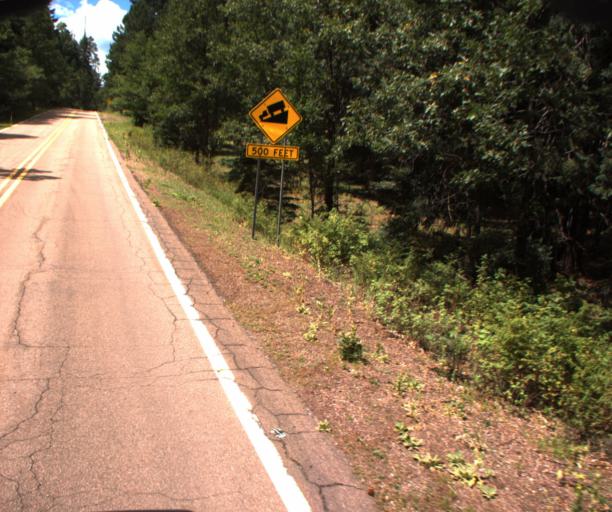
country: US
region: Arizona
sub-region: Navajo County
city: Pinetop-Lakeside
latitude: 34.0283
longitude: -109.7653
